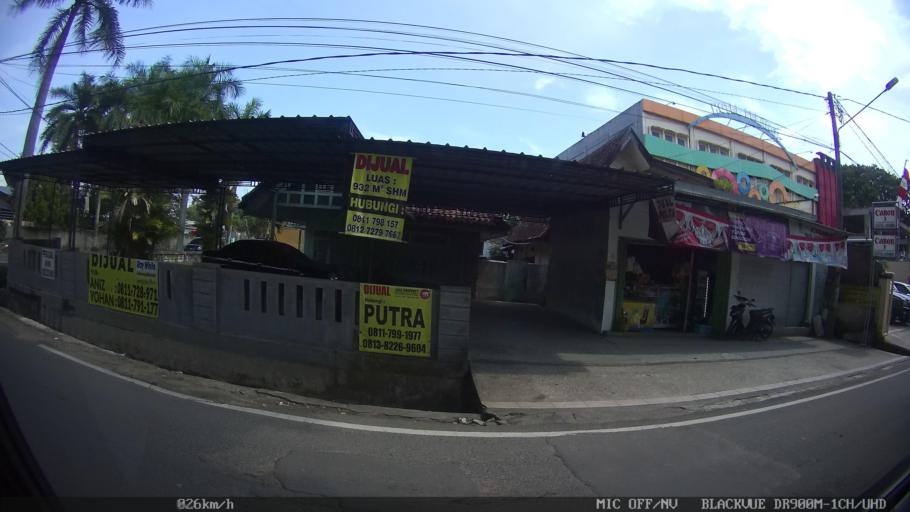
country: ID
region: Lampung
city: Bandarlampung
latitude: -5.4178
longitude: 105.2609
